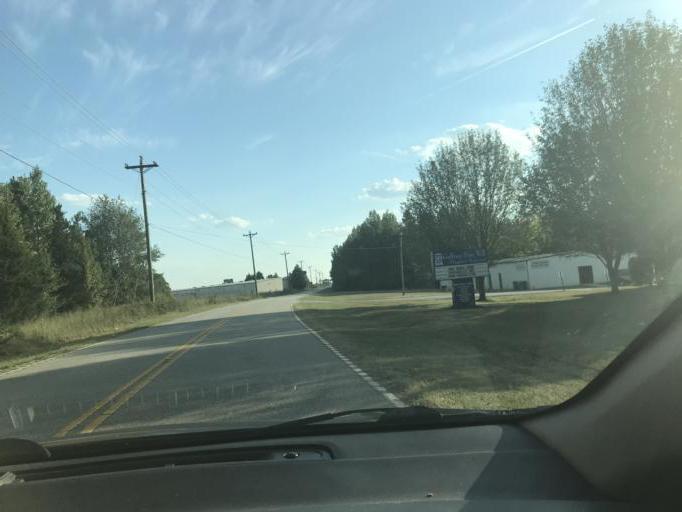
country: US
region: South Carolina
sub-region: Cherokee County
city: Gaffney
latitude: 35.0959
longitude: -81.6896
